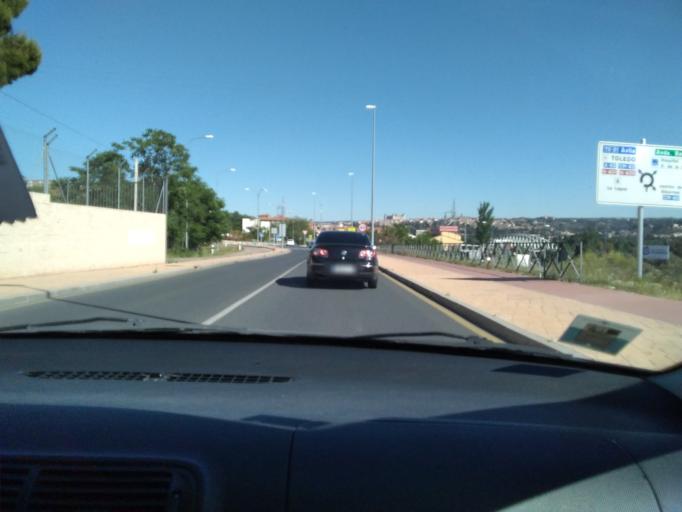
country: ES
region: Castille-La Mancha
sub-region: Province of Toledo
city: Toledo
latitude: 39.8799
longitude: -4.0491
